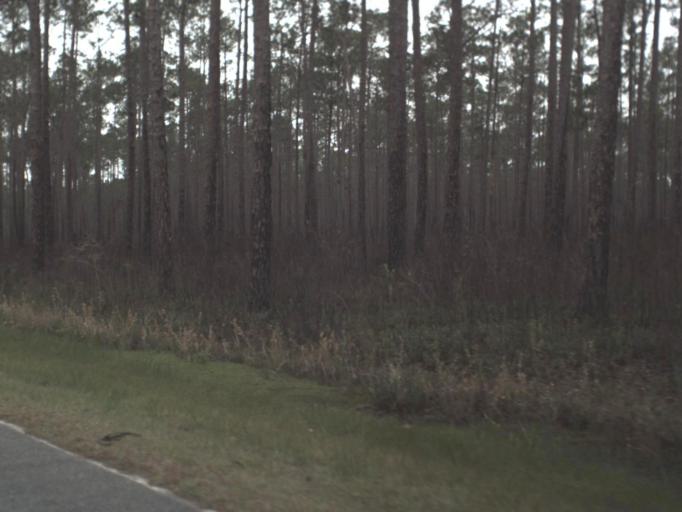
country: US
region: Florida
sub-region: Franklin County
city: Apalachicola
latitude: 29.9467
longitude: -84.9765
